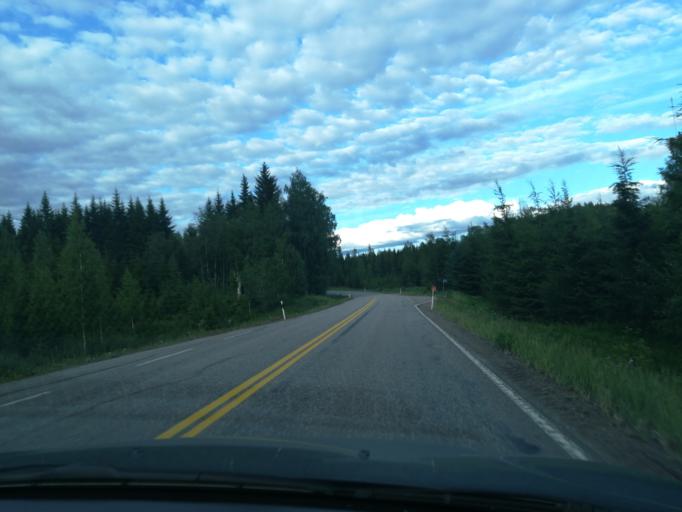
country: FI
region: Southern Savonia
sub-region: Mikkeli
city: Puumala
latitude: 61.5234
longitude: 27.9295
